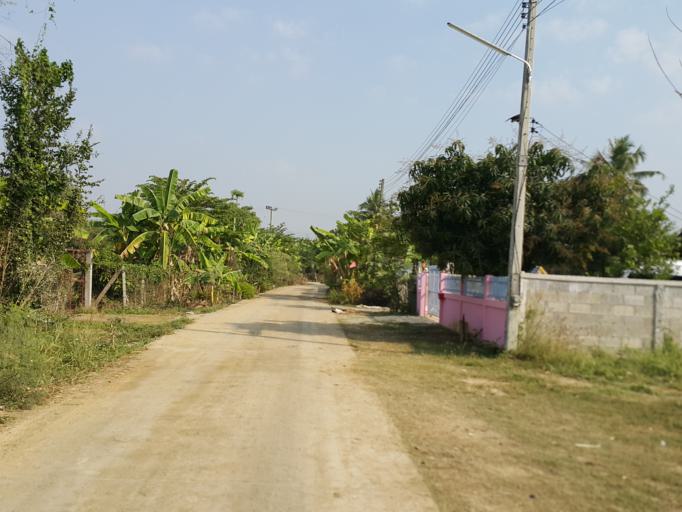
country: TH
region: Chiang Mai
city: San Kamphaeng
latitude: 18.7772
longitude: 99.0981
